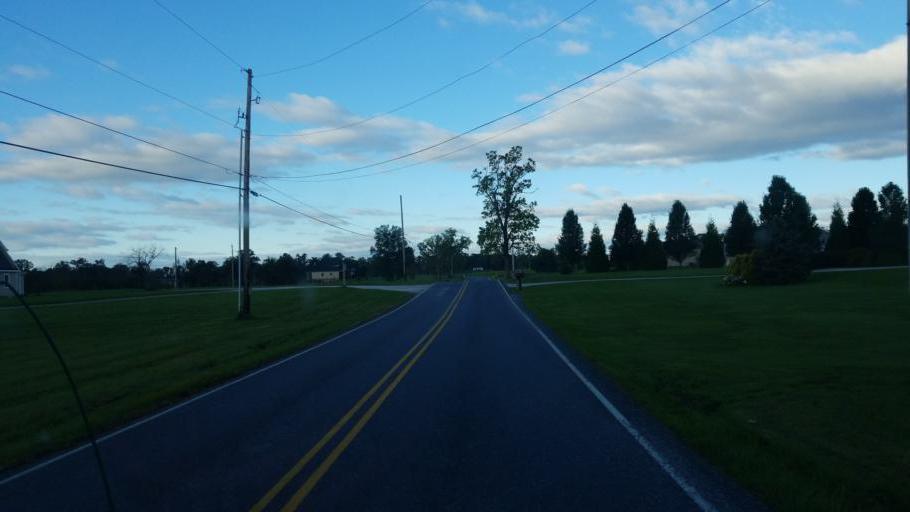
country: US
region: Pennsylvania
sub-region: Adams County
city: New Oxford
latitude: 39.8973
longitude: -77.1068
